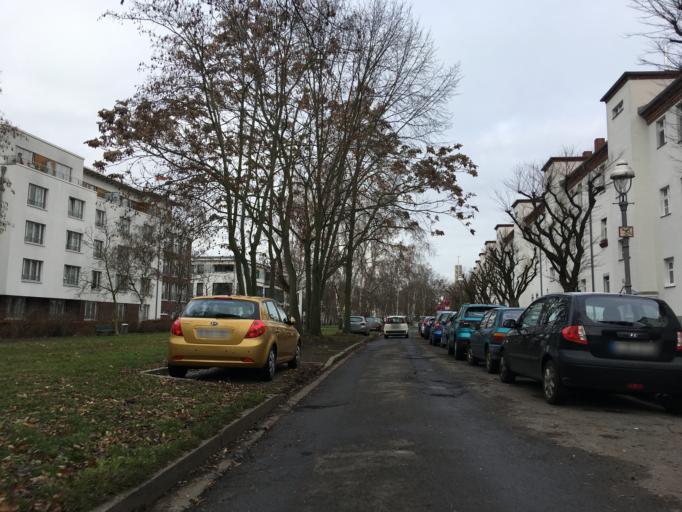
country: DE
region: Berlin
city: Wittenau
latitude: 52.5887
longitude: 13.3298
